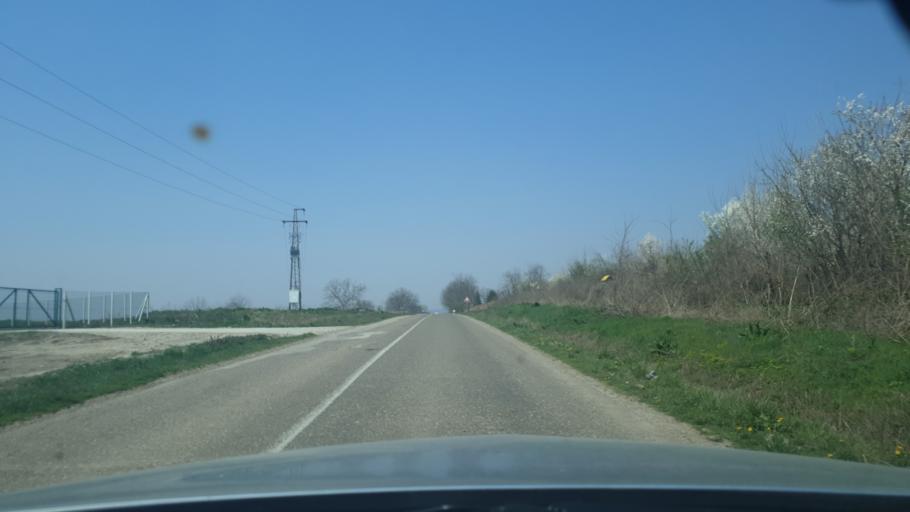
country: RS
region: Autonomna Pokrajina Vojvodina
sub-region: Sremski Okrug
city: Ruma
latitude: 45.0108
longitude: 19.7841
